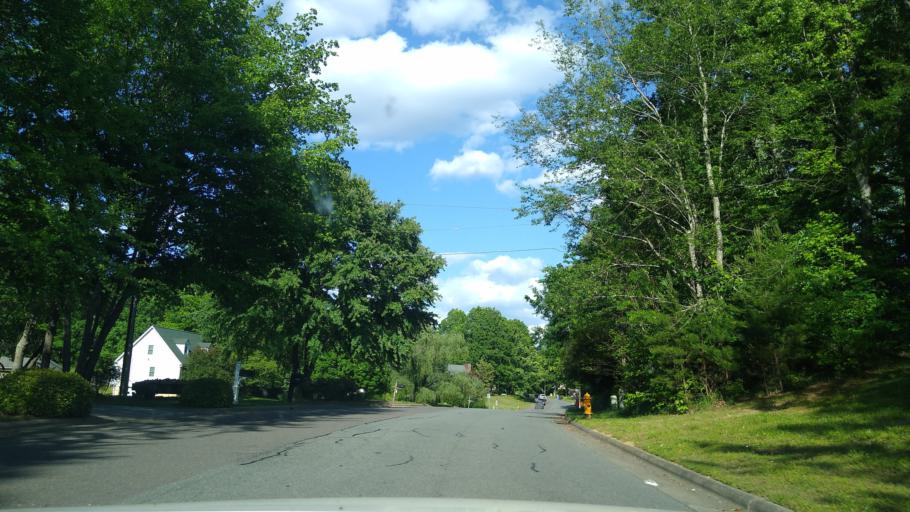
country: US
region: North Carolina
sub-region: Forsyth County
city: Kernersville
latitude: 36.1036
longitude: -80.0843
